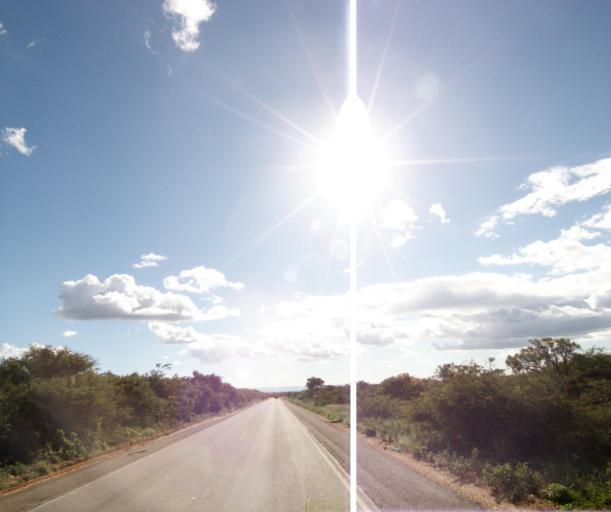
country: BR
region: Bahia
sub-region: Caetite
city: Caetite
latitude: -14.1311
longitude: -42.6300
